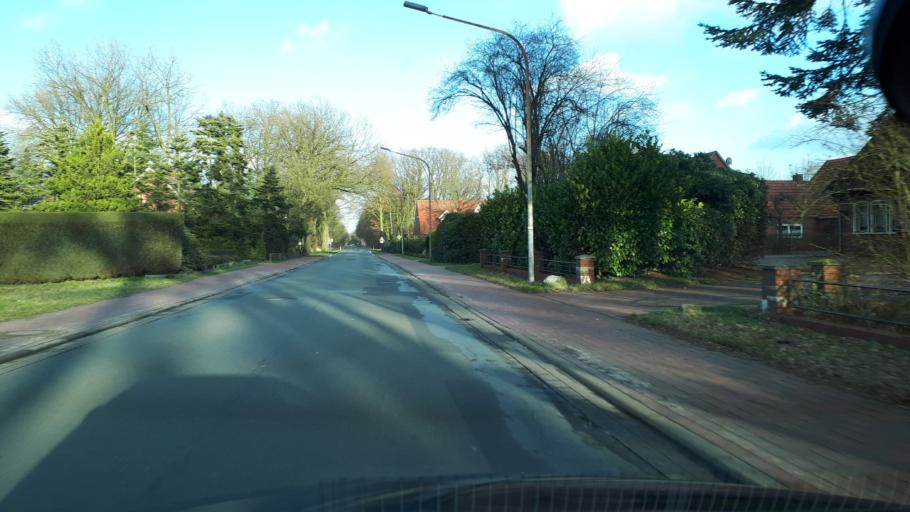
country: DE
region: Lower Saxony
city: Vrees
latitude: 52.8825
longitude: 7.8443
